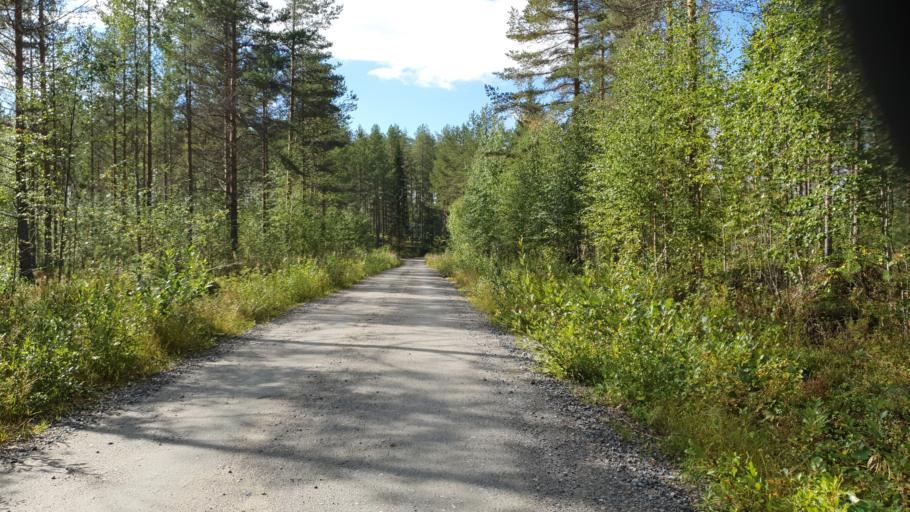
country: FI
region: Kainuu
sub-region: Kehys-Kainuu
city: Kuhmo
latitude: 64.1309
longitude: 29.3506
